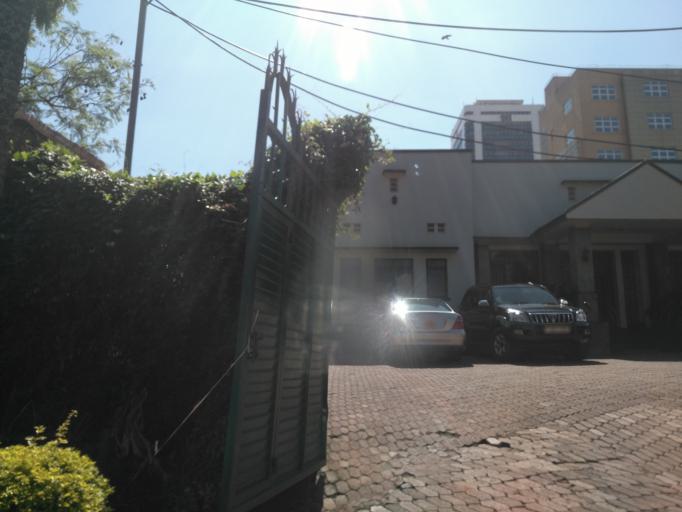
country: UG
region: Central Region
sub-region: Kampala District
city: Kampala
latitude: 0.3185
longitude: 32.5902
